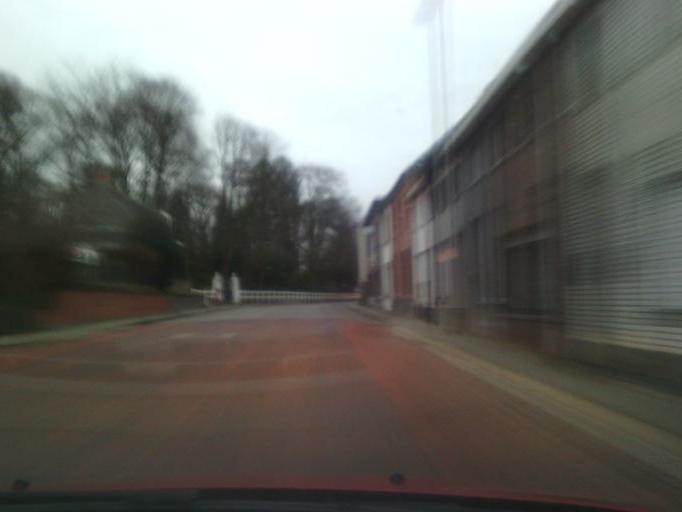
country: BE
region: Flanders
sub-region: Provincie Oost-Vlaanderen
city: Waasmunster
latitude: 51.1119
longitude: 4.0914
